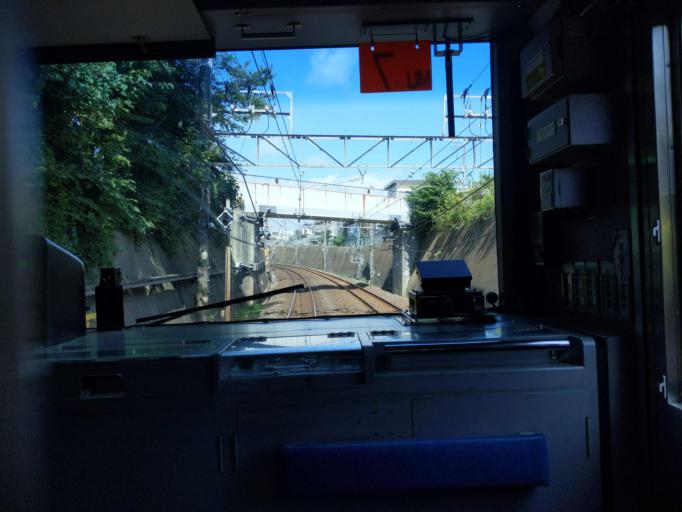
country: JP
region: Chiba
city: Funabashi
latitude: 35.7265
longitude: 139.9683
